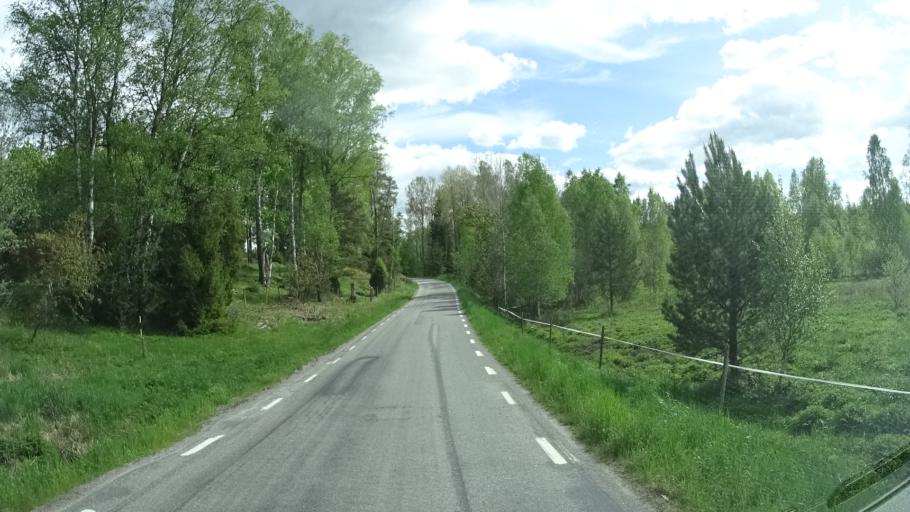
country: SE
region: OEstergoetland
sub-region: Finspangs Kommun
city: Finspang
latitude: 58.6093
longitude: 15.7391
